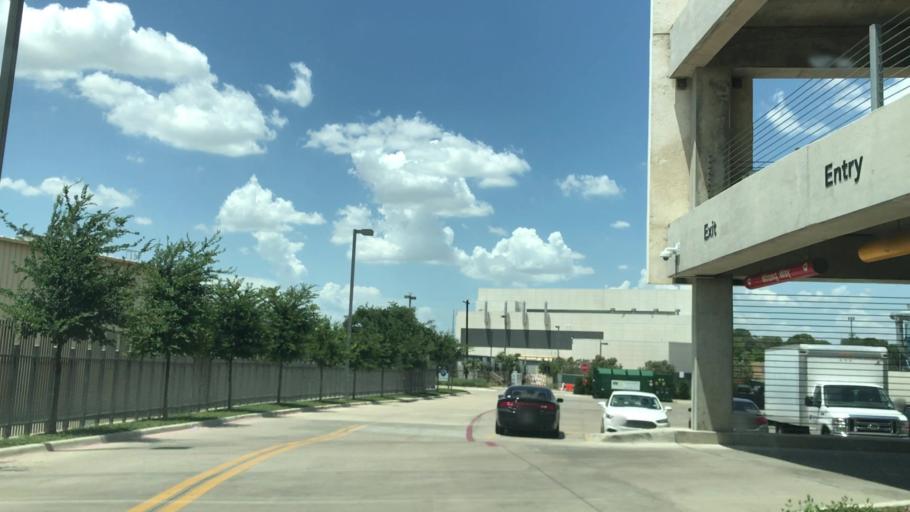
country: US
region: Texas
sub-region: Dallas County
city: Dallas
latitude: 32.8189
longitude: -96.8504
